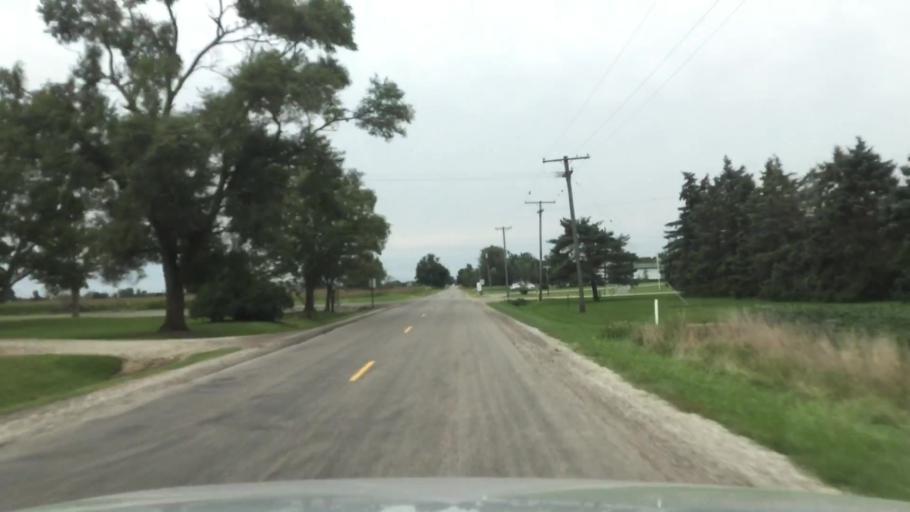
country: US
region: Michigan
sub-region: Washtenaw County
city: Milan
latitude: 42.0766
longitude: -83.7356
